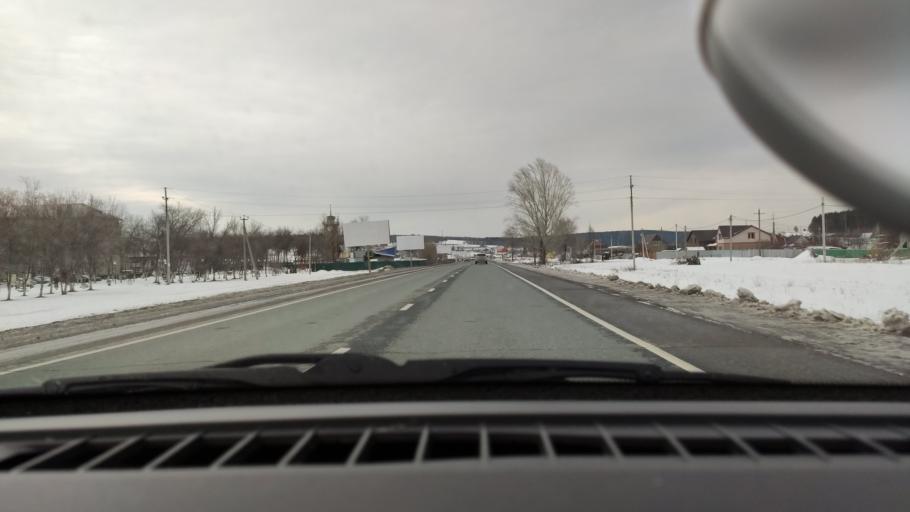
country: RU
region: Samara
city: Kurumoch
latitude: 53.4847
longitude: 50.0244
